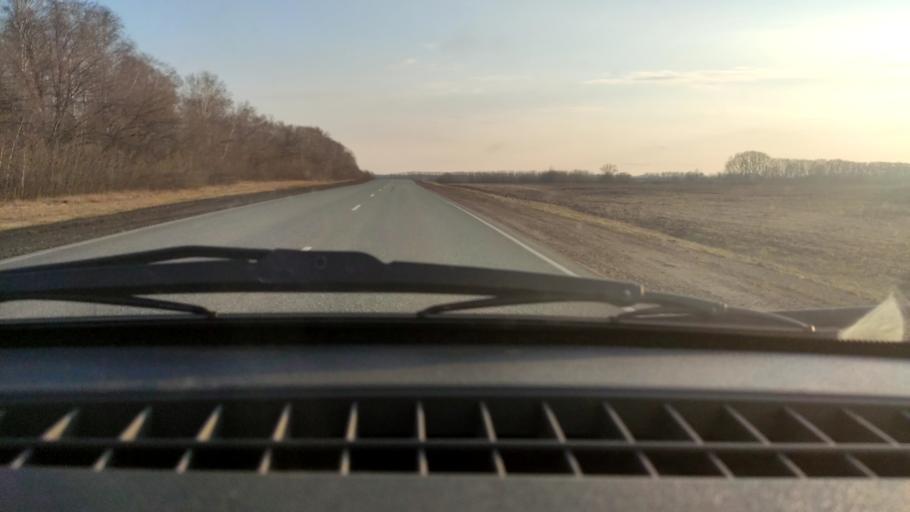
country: RU
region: Bashkortostan
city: Chishmy
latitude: 54.5318
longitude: 55.3074
